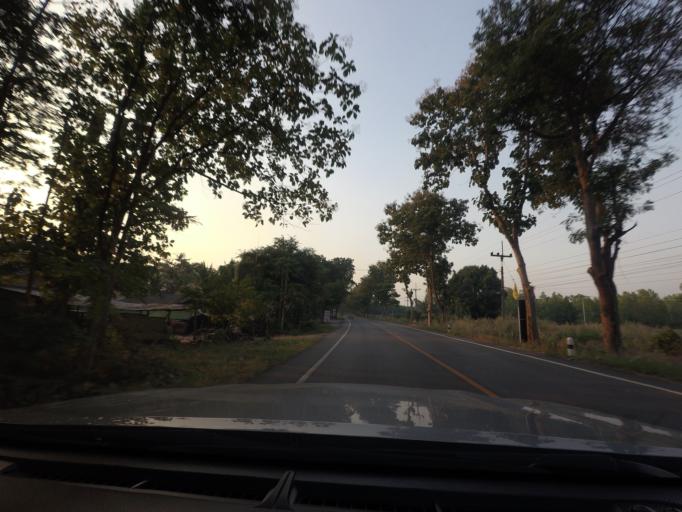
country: TH
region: Phitsanulok
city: Wang Thong
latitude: 16.7322
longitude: 100.4547
